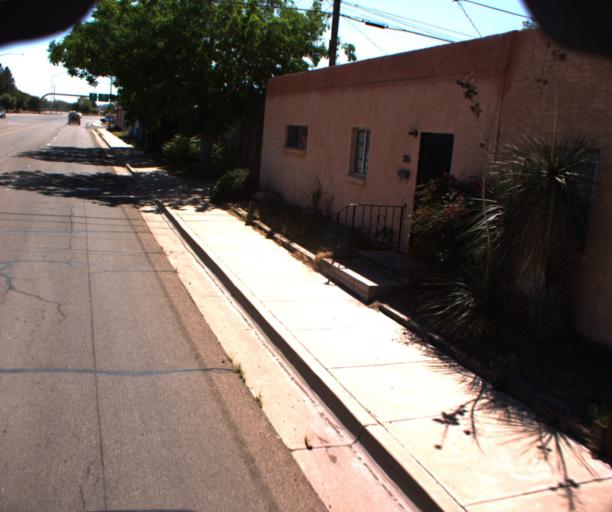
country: US
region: Arizona
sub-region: Cochise County
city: Pirtleville
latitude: 31.3506
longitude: -109.5588
